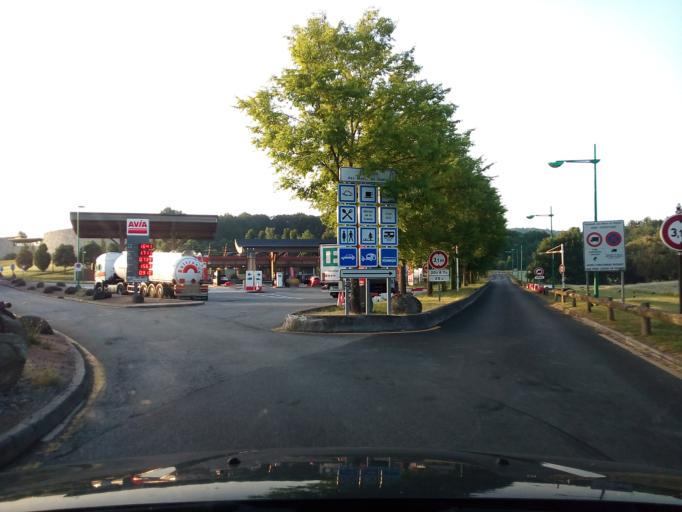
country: FR
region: Limousin
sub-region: Departement de la Creuse
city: Saint-Sulpice-le-Gueretois
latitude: 46.1834
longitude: 1.8449
